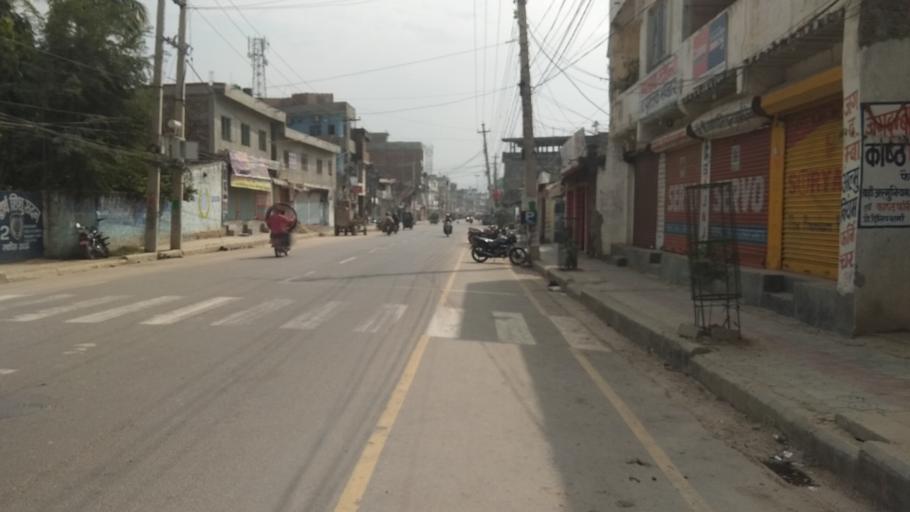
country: NP
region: Central Region
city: Janakpur
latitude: 26.7336
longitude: 85.9326
